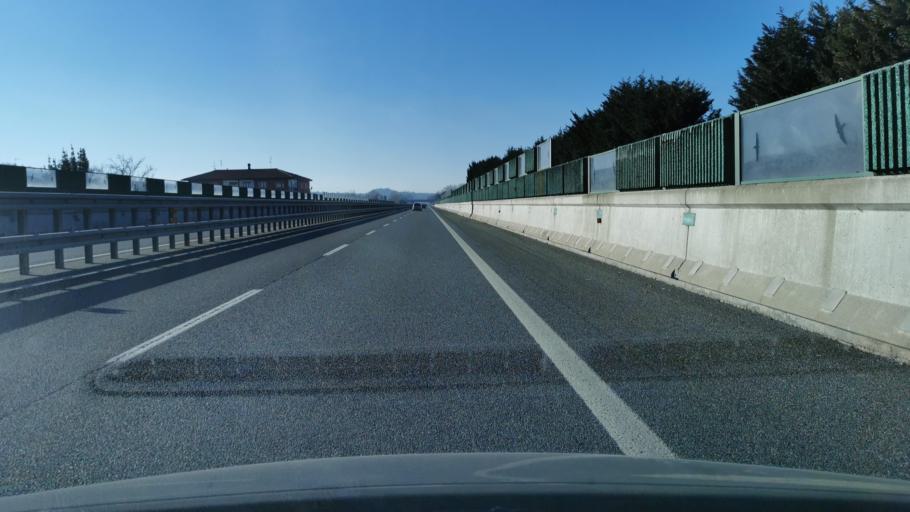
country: IT
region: Piedmont
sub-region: Provincia di Asti
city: Baldichieri d'Asti
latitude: 44.9050
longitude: 8.0914
